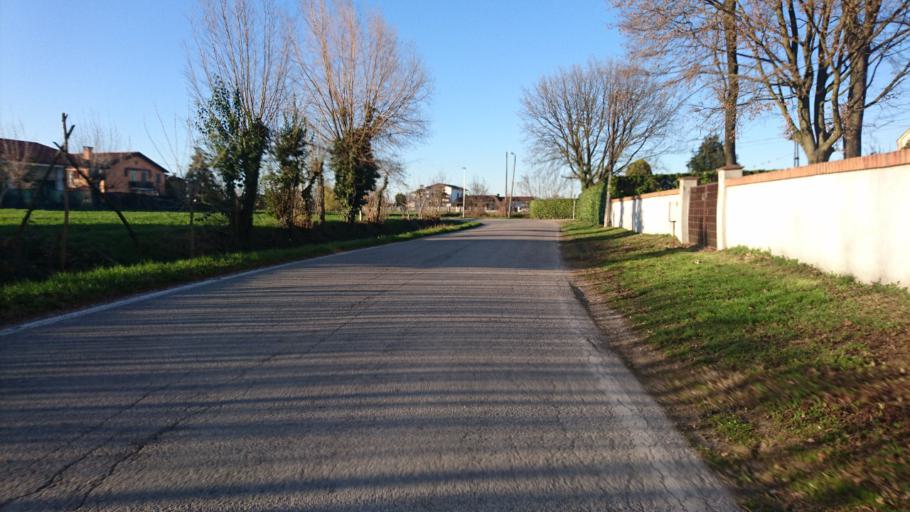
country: IT
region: Veneto
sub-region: Provincia di Padova
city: Bertipaglia
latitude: 45.3046
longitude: 11.8848
